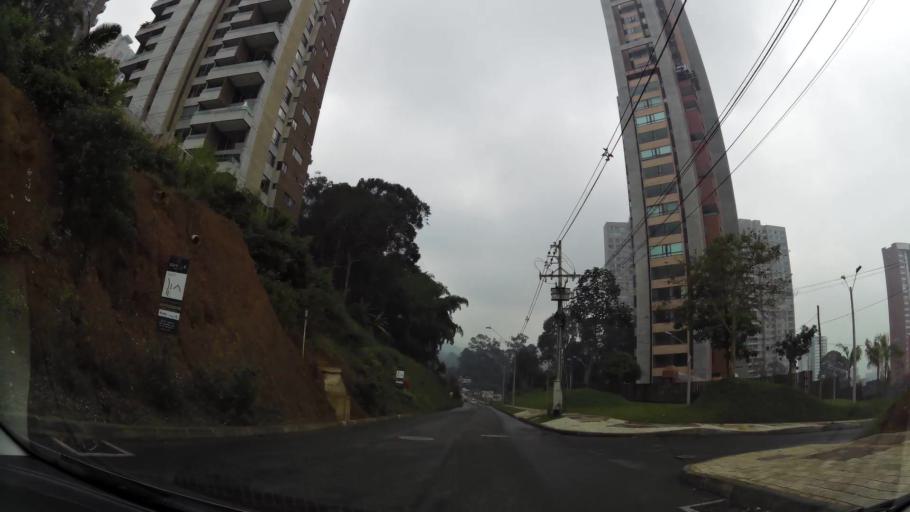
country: CO
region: Antioquia
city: Envigado
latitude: 6.1846
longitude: -75.5586
